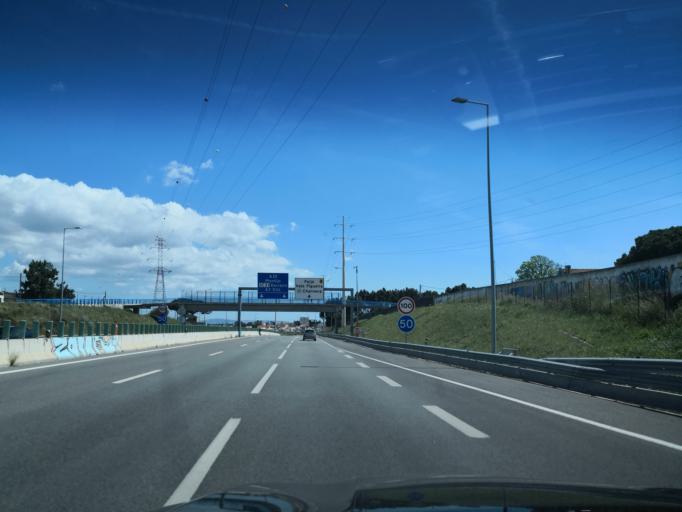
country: PT
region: Setubal
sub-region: Almada
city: Charneca
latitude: 38.6279
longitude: -9.1933
